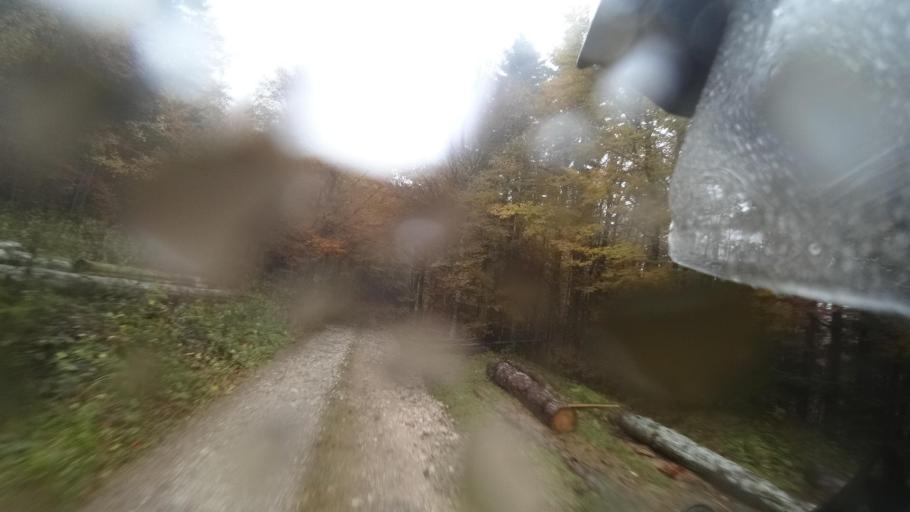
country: HR
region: Primorsko-Goranska
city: Vrbovsko
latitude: 45.2945
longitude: 14.9391
